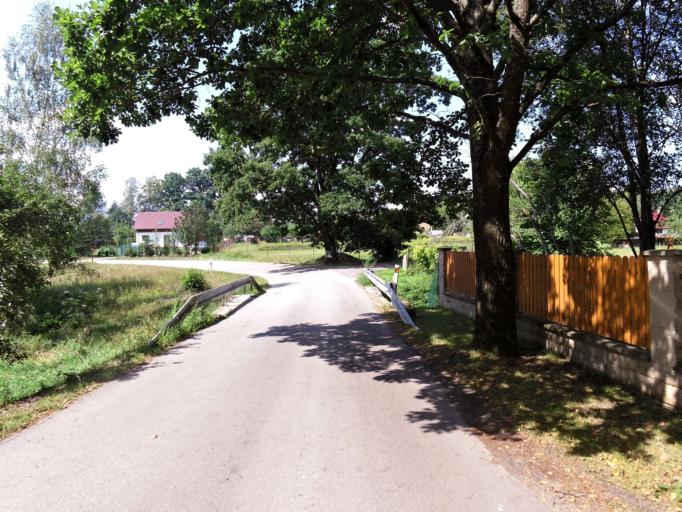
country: CZ
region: Jihocesky
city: Chlum u Trebone
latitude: 48.9799
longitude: 14.9461
